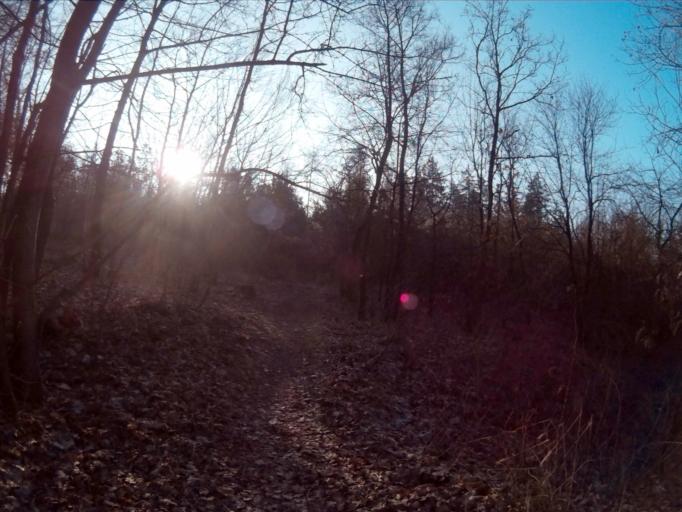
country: CZ
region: Vysocina
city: Namest' nad Oslavou
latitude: 49.1918
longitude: 16.1663
